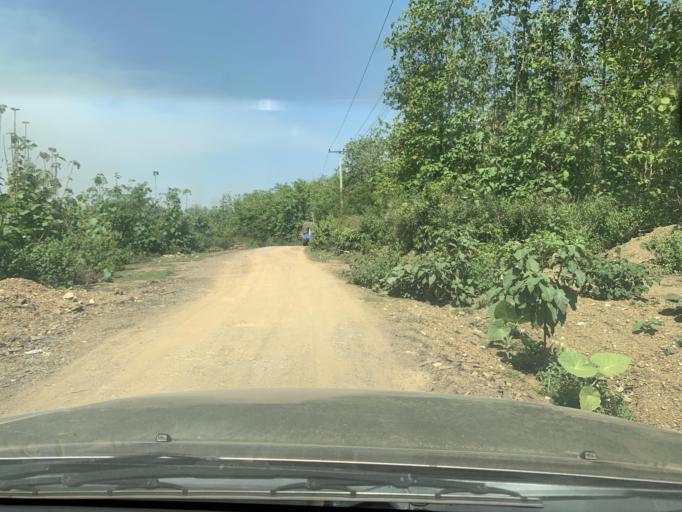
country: LA
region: Louangphabang
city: Louangphabang
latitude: 19.9230
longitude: 102.2715
